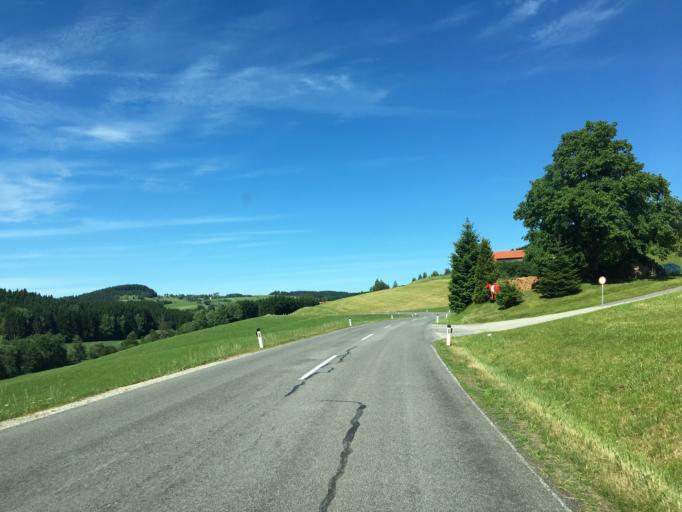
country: AT
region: Upper Austria
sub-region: Politischer Bezirk Urfahr-Umgebung
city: Zwettl an der Rodl
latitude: 48.4538
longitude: 14.2630
